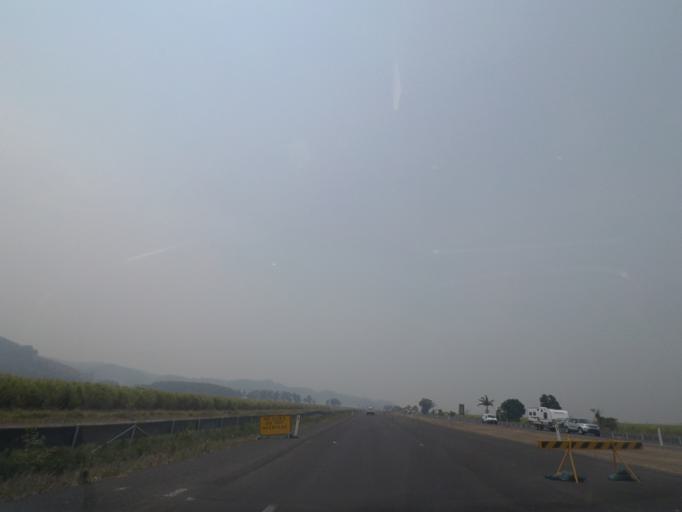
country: AU
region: New South Wales
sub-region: Ballina
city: Ballina
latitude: -28.8978
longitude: 153.4806
